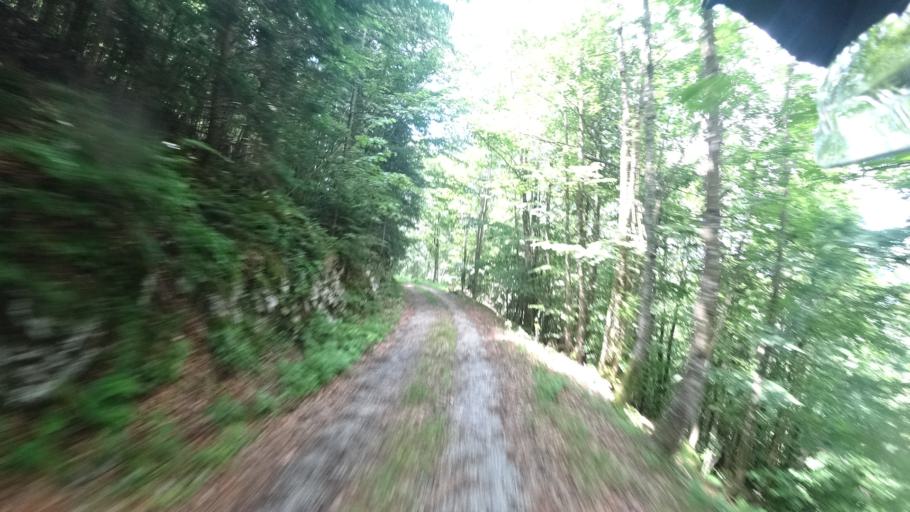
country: SI
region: Osilnica
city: Osilnica
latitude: 45.4965
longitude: 14.7110
